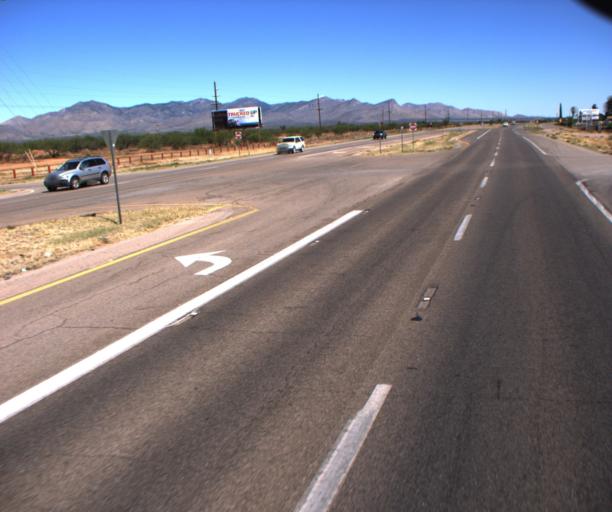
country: US
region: Arizona
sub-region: Cochise County
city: Huachuca City
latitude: 31.6847
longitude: -110.3502
